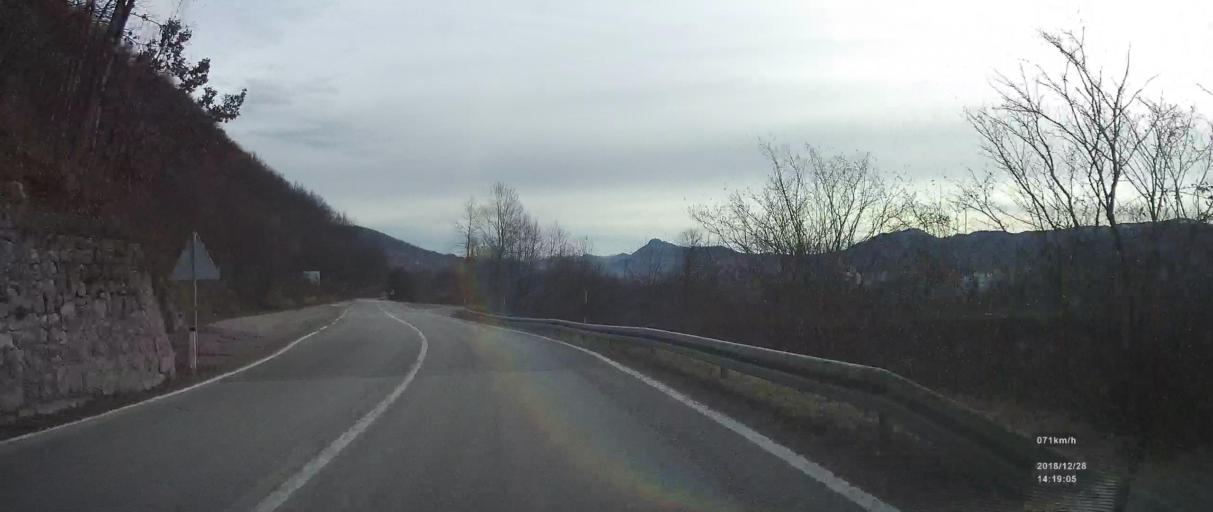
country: HR
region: Primorsko-Goranska
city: Vrbovsko
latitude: 45.4069
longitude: 15.0636
